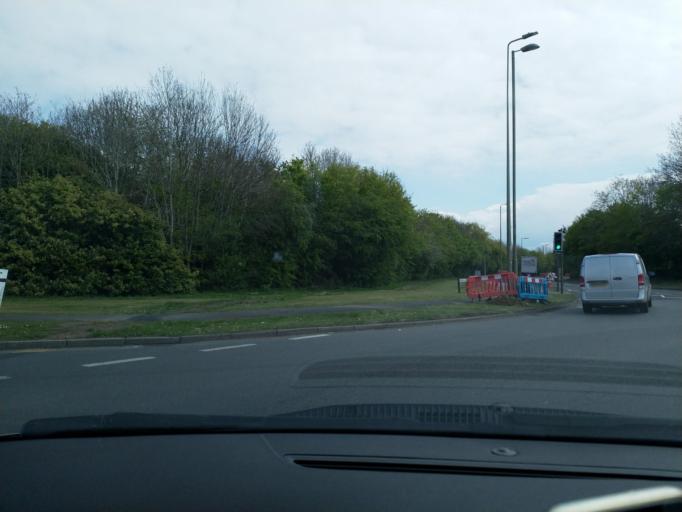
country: GB
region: England
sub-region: Suffolk
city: Woodbridge
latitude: 52.0686
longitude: 1.3163
